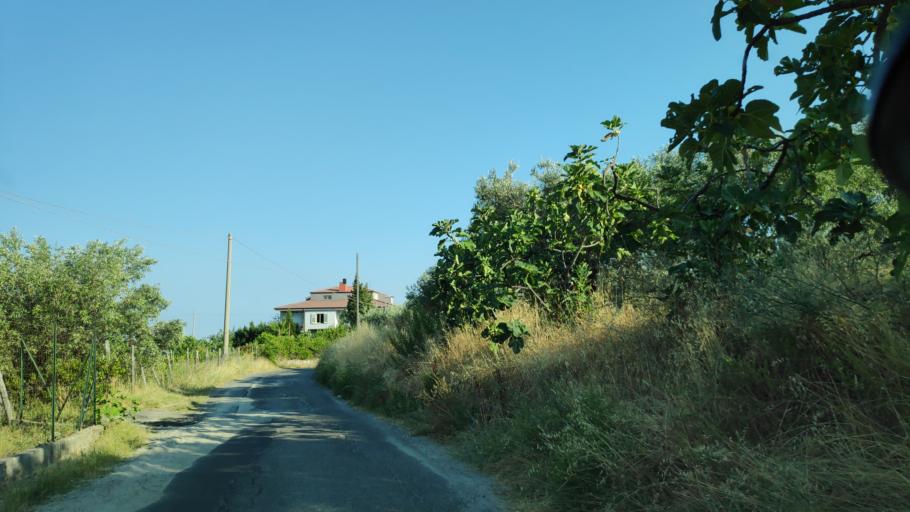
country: IT
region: Calabria
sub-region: Provincia di Catanzaro
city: Guardavalle
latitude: 38.5103
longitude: 16.5039
